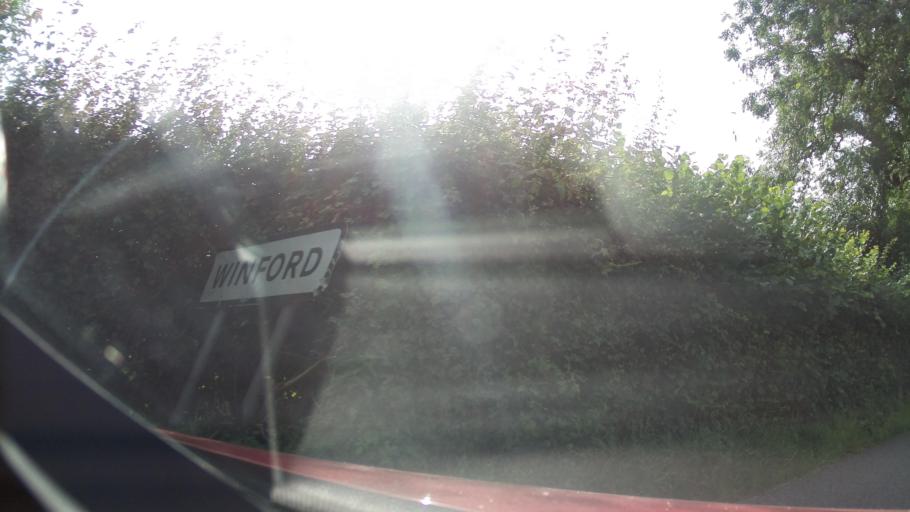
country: GB
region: England
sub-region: North Somerset
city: Winford
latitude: 51.3926
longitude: -2.6642
